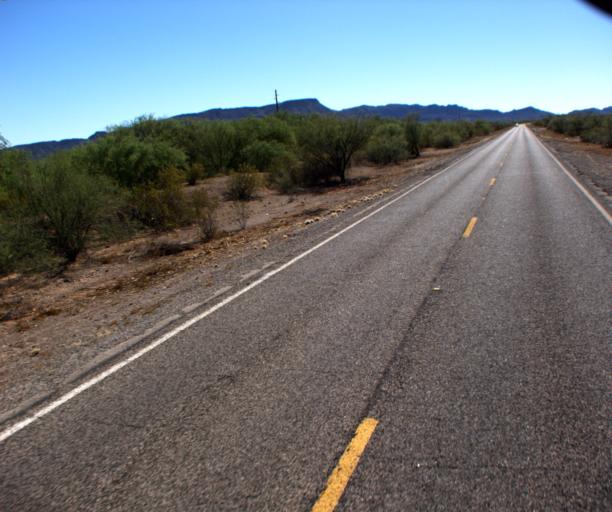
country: US
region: Arizona
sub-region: Pima County
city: Ajo
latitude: 32.3280
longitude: -112.7796
